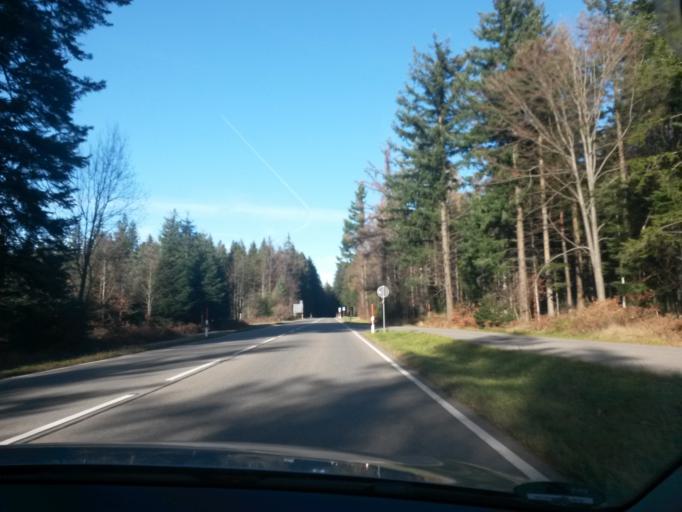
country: DE
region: Baden-Wuerttemberg
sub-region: Karlsruhe Region
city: Baiersbronn
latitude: 48.5293
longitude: 8.4289
